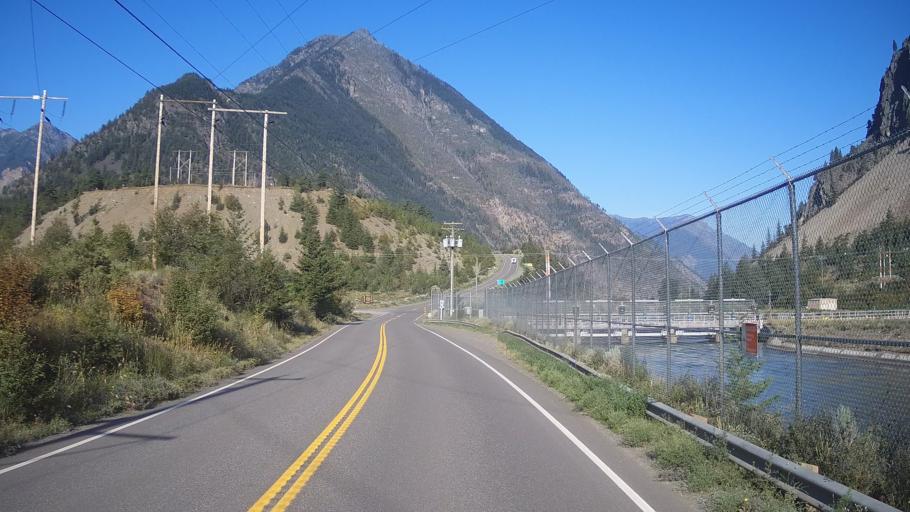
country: CA
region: British Columbia
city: Lillooet
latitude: 50.6690
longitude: -121.9761
